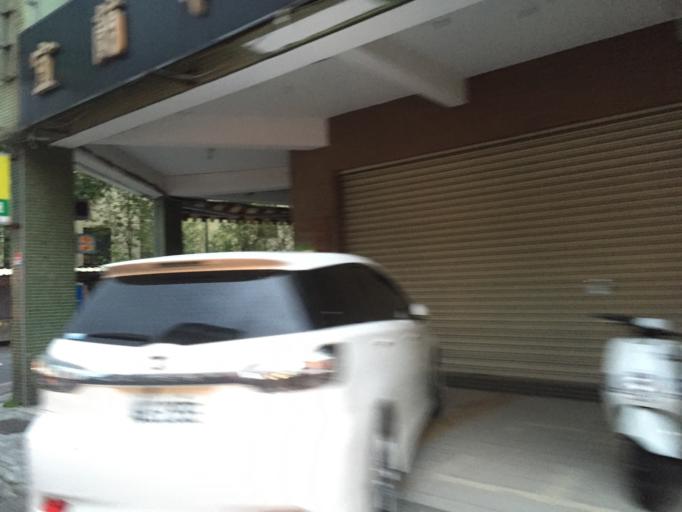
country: TW
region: Taiwan
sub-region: Yilan
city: Yilan
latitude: 24.7554
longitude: 121.7521
